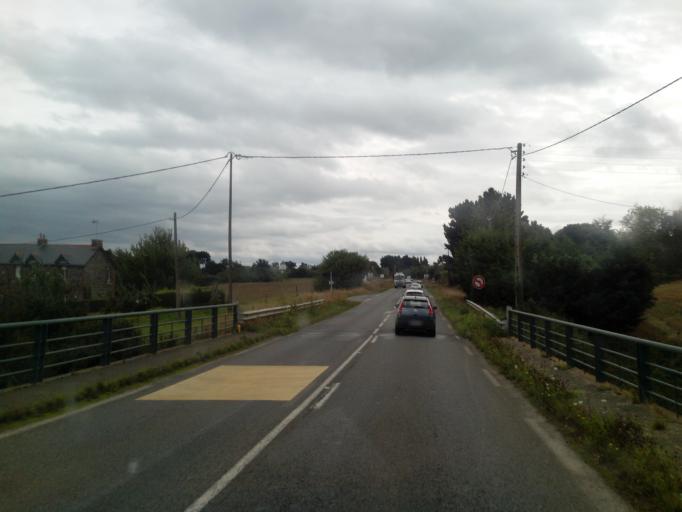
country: FR
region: Brittany
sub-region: Departement des Cotes-d'Armor
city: Etables-sur-Mer
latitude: 48.6236
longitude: -2.8255
